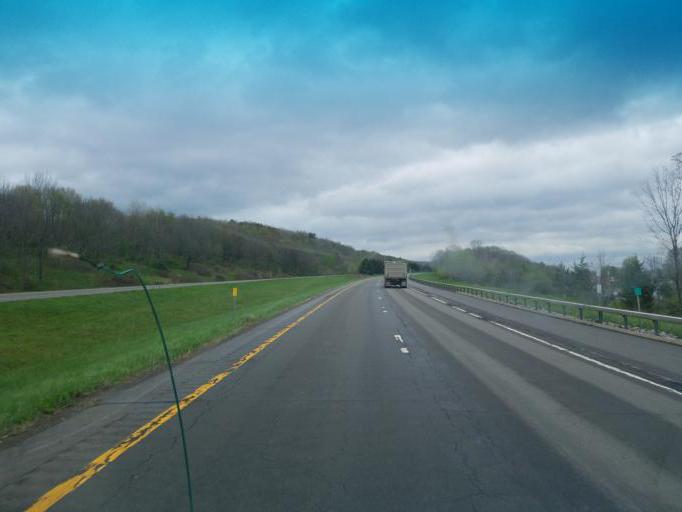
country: US
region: New York
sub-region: Chautauqua County
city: Falconer
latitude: 42.1370
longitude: -79.1762
